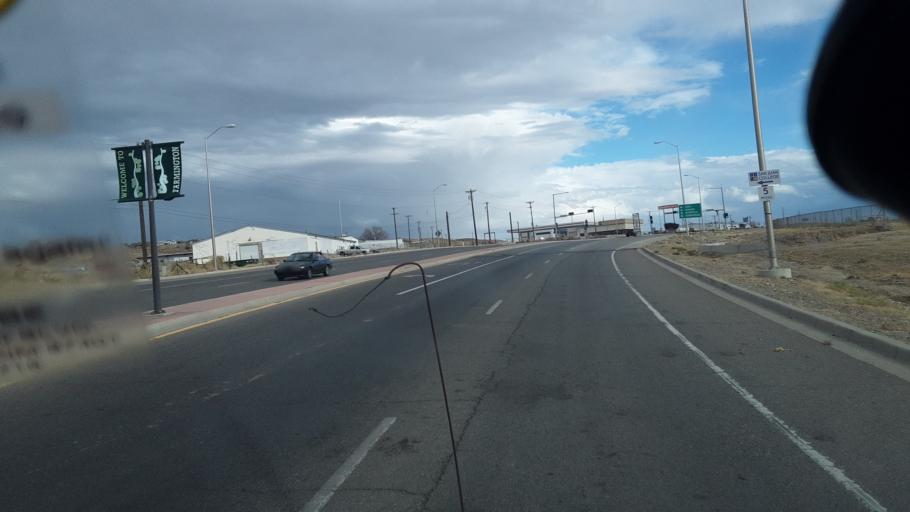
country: US
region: New Mexico
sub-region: San Juan County
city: Farmington
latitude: 36.7190
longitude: -108.1598
